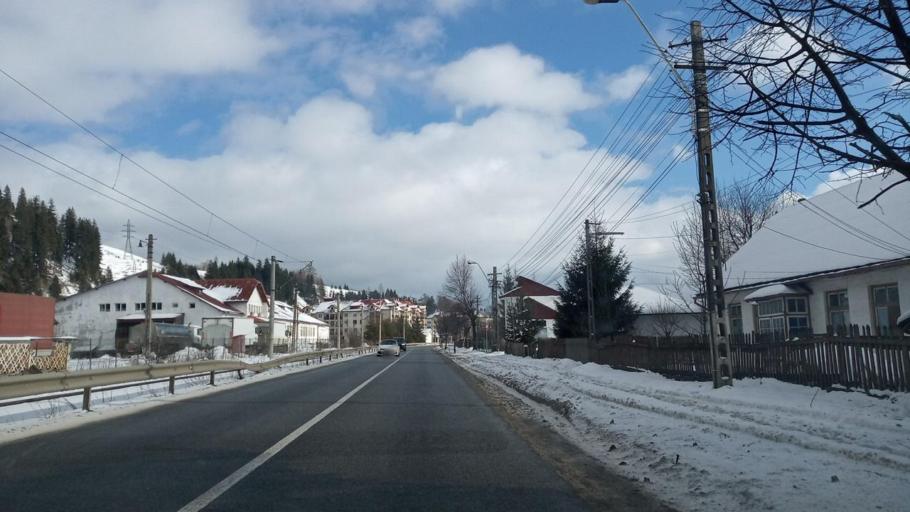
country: RO
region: Suceava
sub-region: Municipiul Vatra Dornei
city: Vatra Dornei
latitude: 47.3487
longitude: 25.3337
